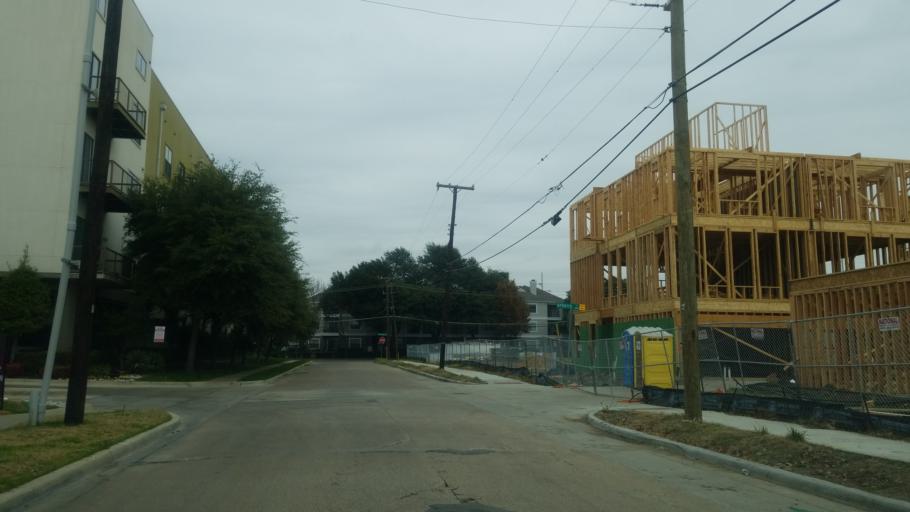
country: US
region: Texas
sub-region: Dallas County
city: Highland Park
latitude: 32.8161
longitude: -96.8193
